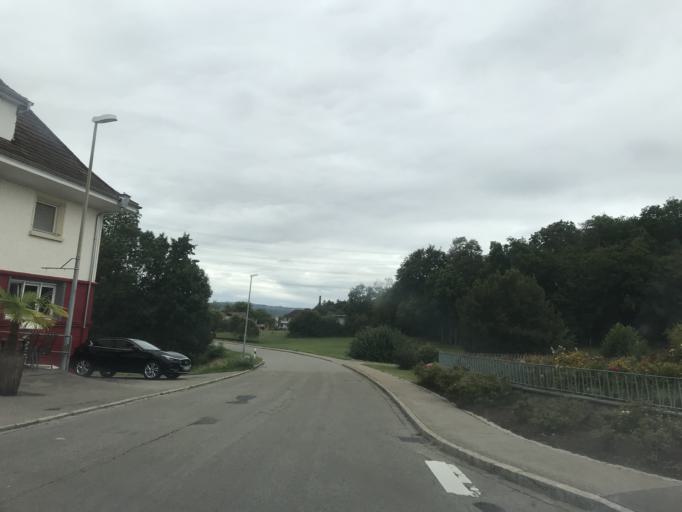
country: DE
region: Baden-Wuerttemberg
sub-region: Freiburg Region
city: Murg
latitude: 47.5647
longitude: 8.0329
